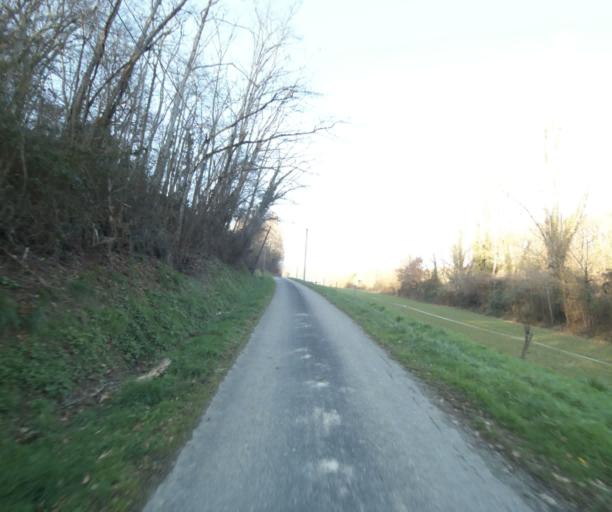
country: FR
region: Midi-Pyrenees
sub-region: Departement du Tarn-et-Garonne
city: Moissac
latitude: 44.1323
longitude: 1.1314
